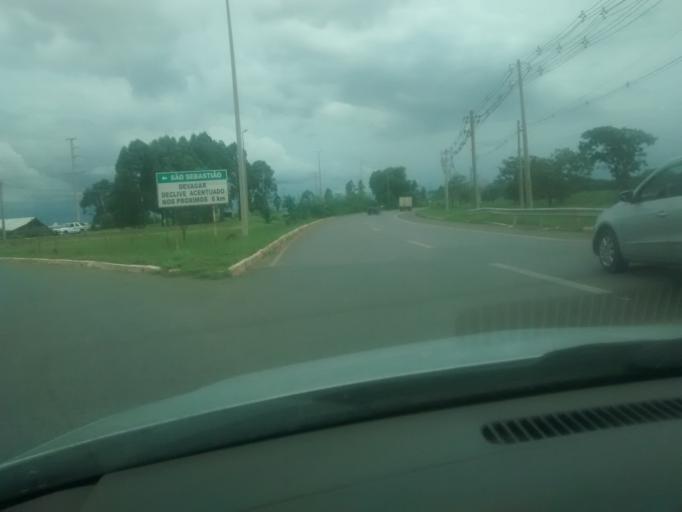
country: BR
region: Federal District
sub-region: Brasilia
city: Brasilia
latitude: -15.8857
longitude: -47.8223
